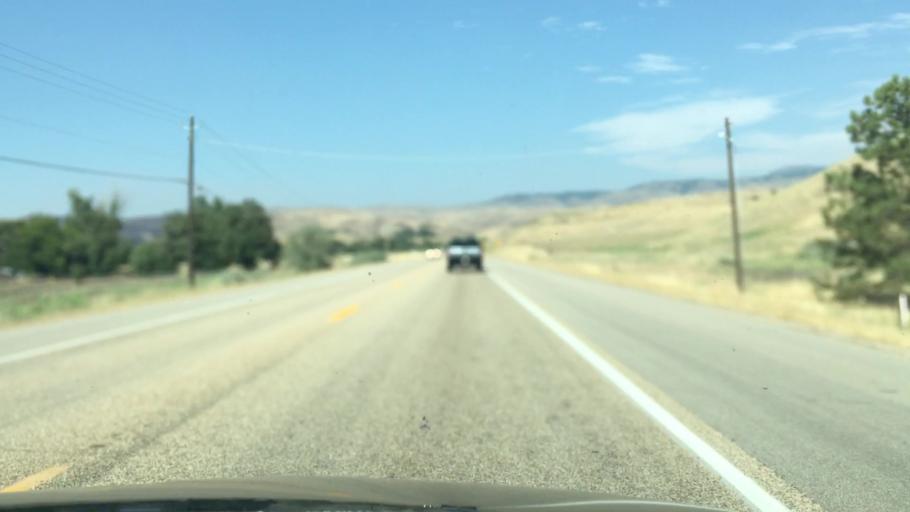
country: US
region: Idaho
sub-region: Ada County
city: Eagle
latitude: 43.7260
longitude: -116.3109
